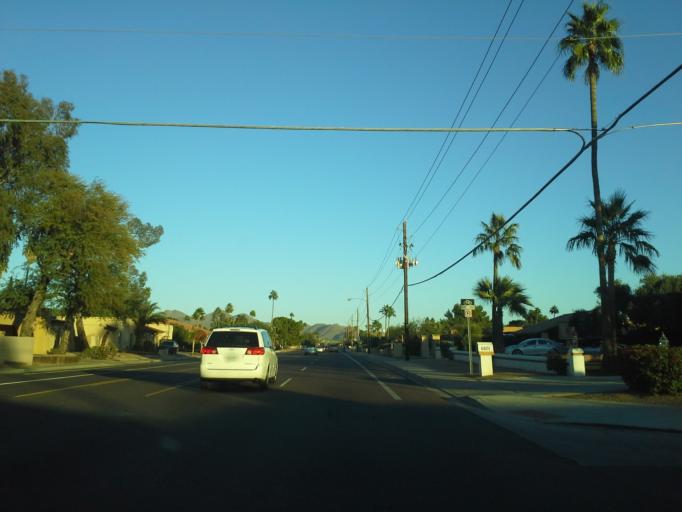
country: US
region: Arizona
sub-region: Maricopa County
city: Paradise Valley
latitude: 33.6112
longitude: -111.9346
